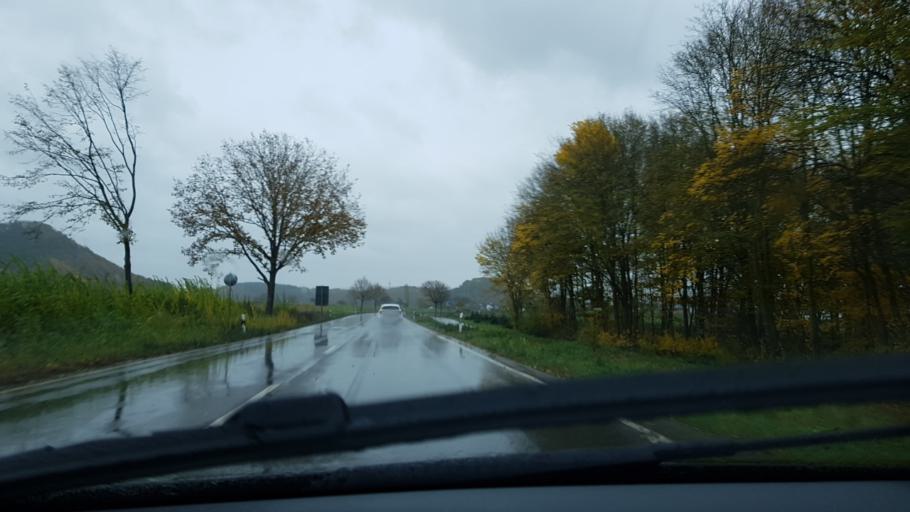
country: DE
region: Rheinland-Pfalz
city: Neuerburg
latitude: 49.9924
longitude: 6.9309
